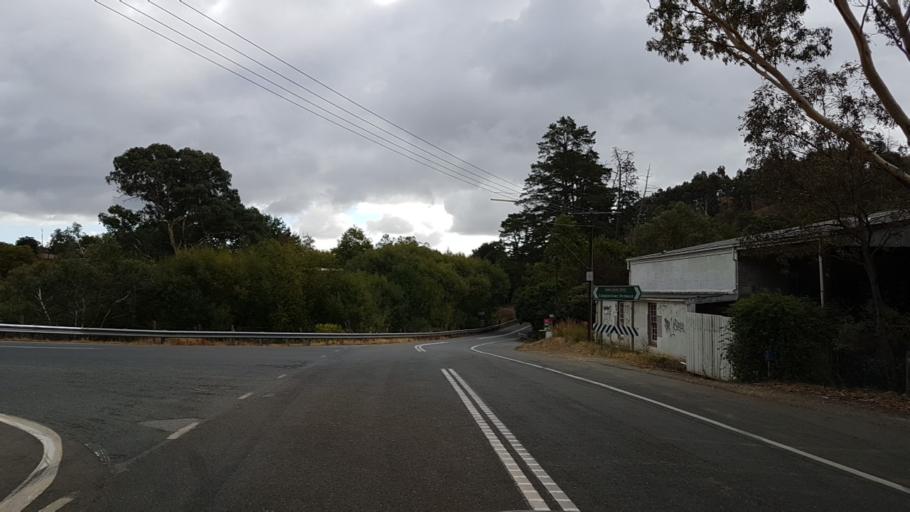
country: AU
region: South Australia
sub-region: Adelaide Hills
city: Gumeracha
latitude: -34.8413
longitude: 138.8320
